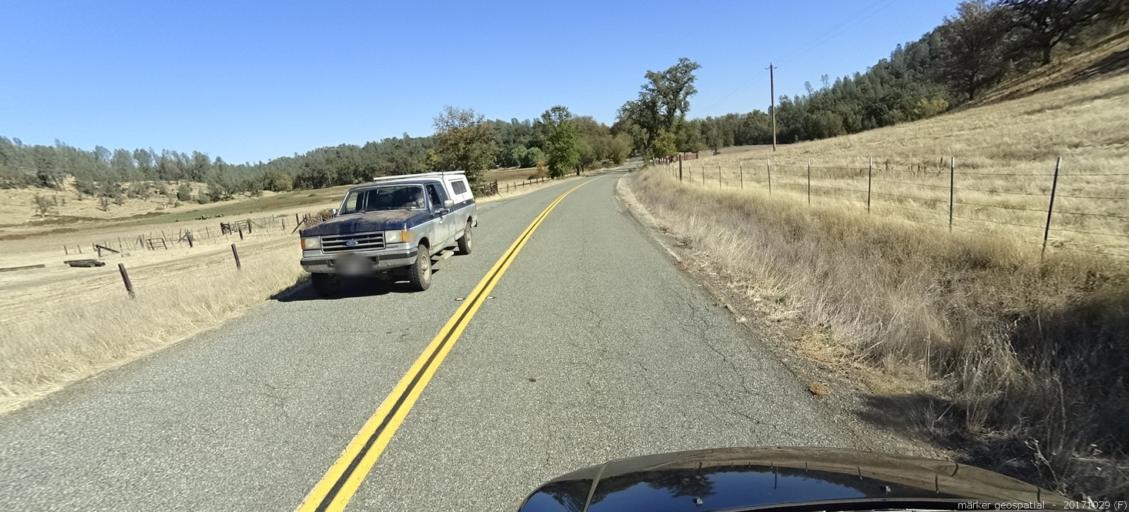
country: US
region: California
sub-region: Shasta County
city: Shasta
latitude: 40.4789
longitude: -122.5926
